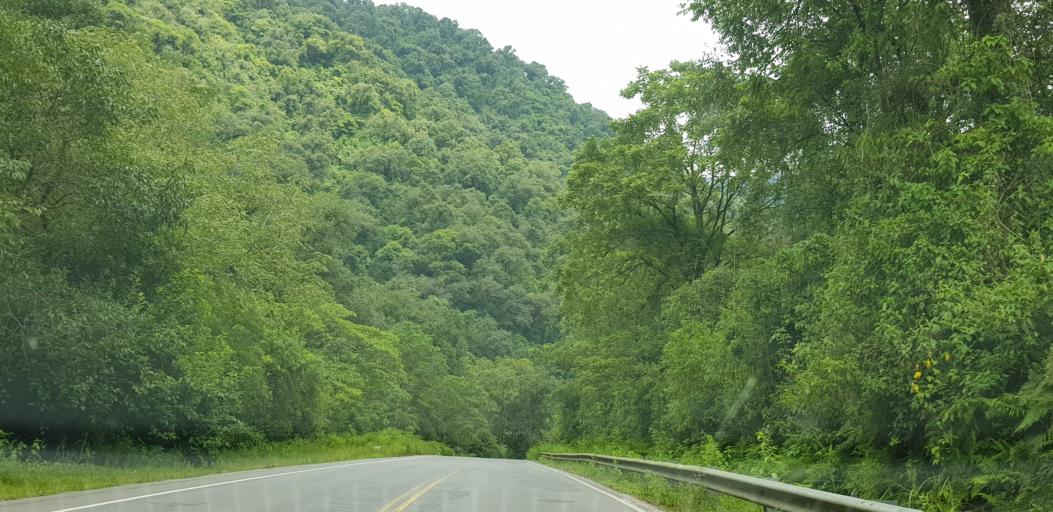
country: AR
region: Tucuman
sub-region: Departamento de Monteros
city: Monteros
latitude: -27.0889
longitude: -65.6606
